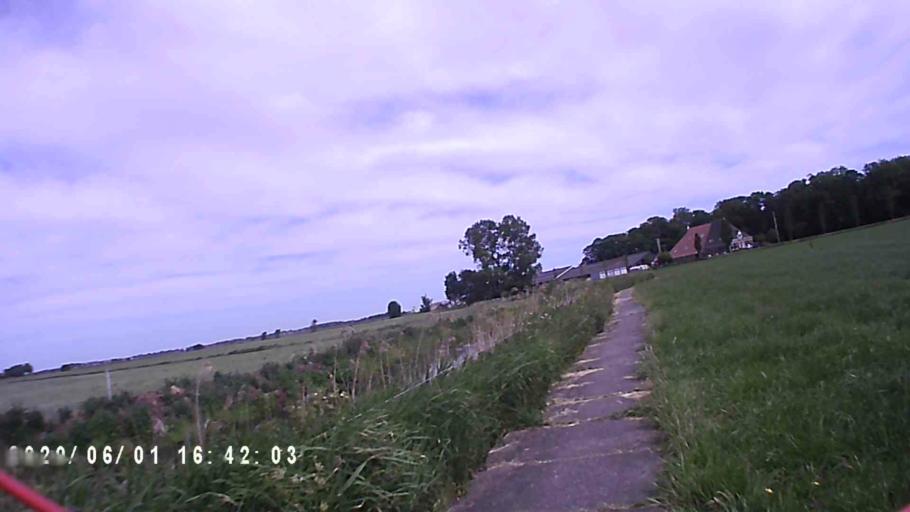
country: NL
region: Friesland
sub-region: Gemeente Boarnsterhim
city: Warten
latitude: 53.1834
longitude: 5.8785
